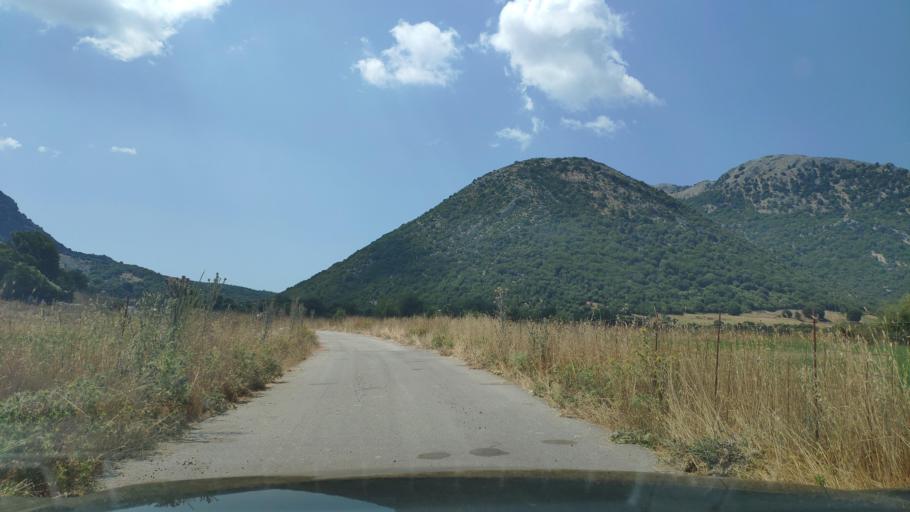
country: GR
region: West Greece
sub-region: Nomos Aitolias kai Akarnanias
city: Monastirakion
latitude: 38.7786
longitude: 20.9719
